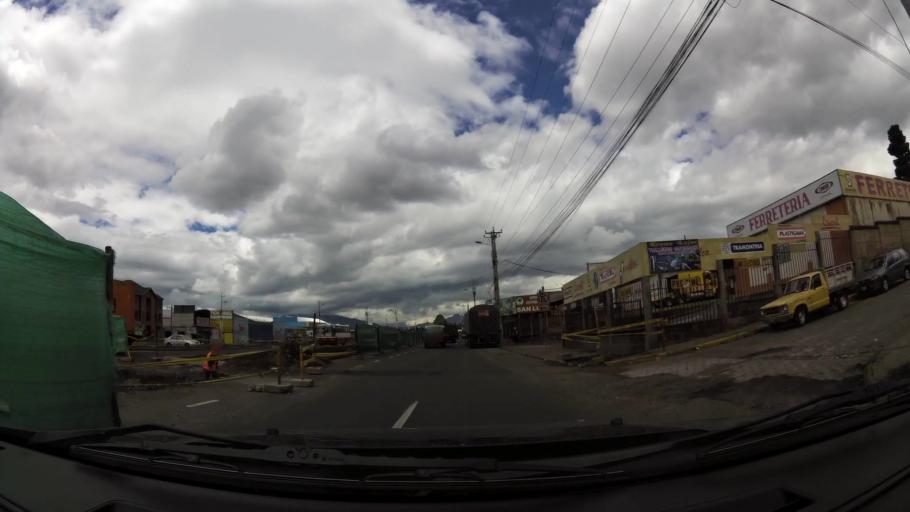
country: EC
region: Pichincha
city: Sangolqui
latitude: -0.3402
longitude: -78.5493
